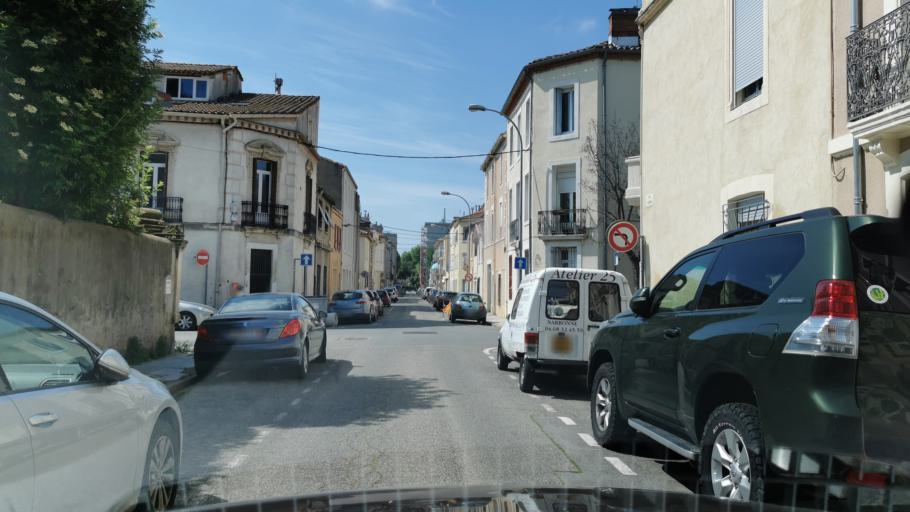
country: FR
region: Languedoc-Roussillon
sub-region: Departement de l'Aude
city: Narbonne
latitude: 43.1831
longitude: 3.0104
